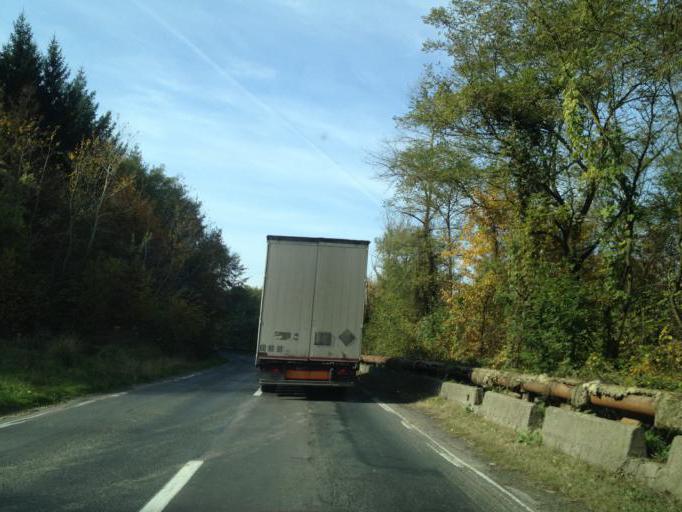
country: RO
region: Hunedoara
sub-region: Comuna Ilia
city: Ilia
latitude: 45.9183
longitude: 22.6365
